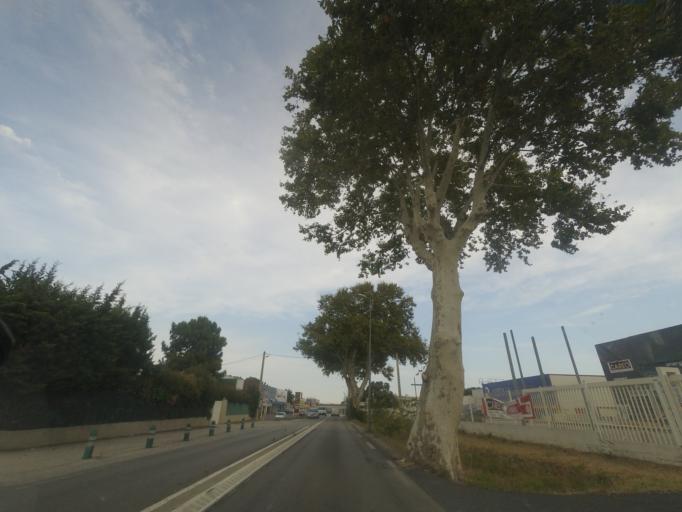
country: FR
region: Languedoc-Roussillon
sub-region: Departement des Pyrenees-Orientales
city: Saint-Esteve
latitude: 42.6955
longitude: 2.8596
